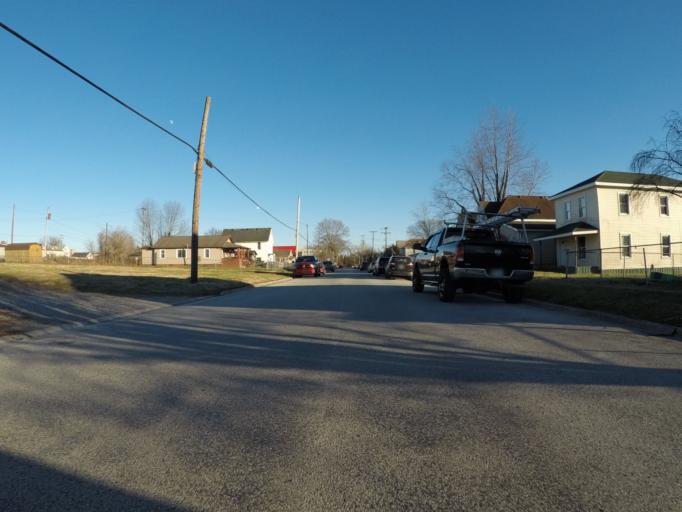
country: US
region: West Virginia
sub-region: Wayne County
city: Kenova
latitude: 38.3986
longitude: -82.5825
